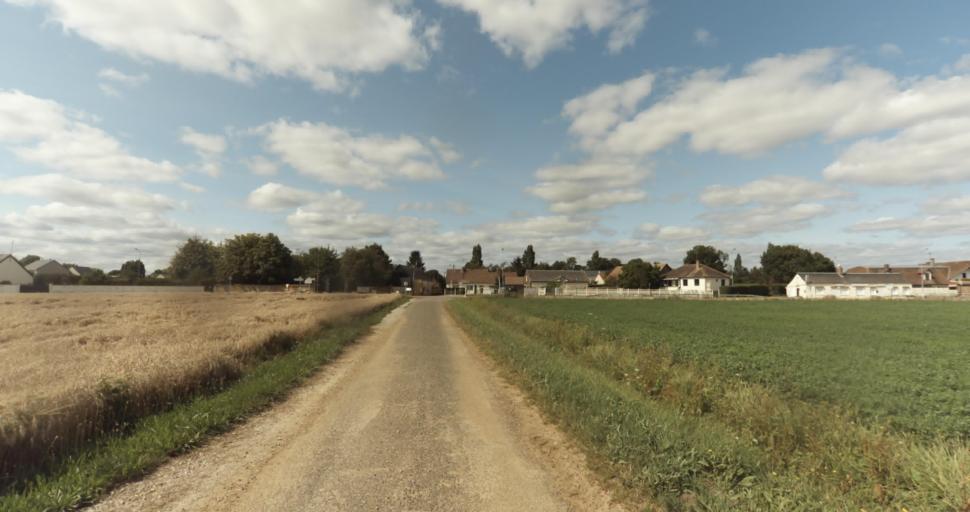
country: FR
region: Haute-Normandie
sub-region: Departement de l'Eure
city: Marcilly-sur-Eure
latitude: 48.8982
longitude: 1.2393
